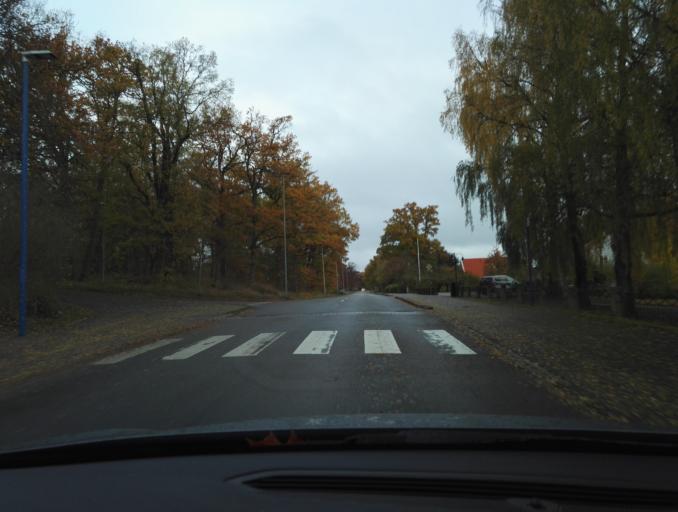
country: SE
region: Kronoberg
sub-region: Vaxjo Kommun
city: Vaexjoe
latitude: 56.9105
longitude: 14.7392
